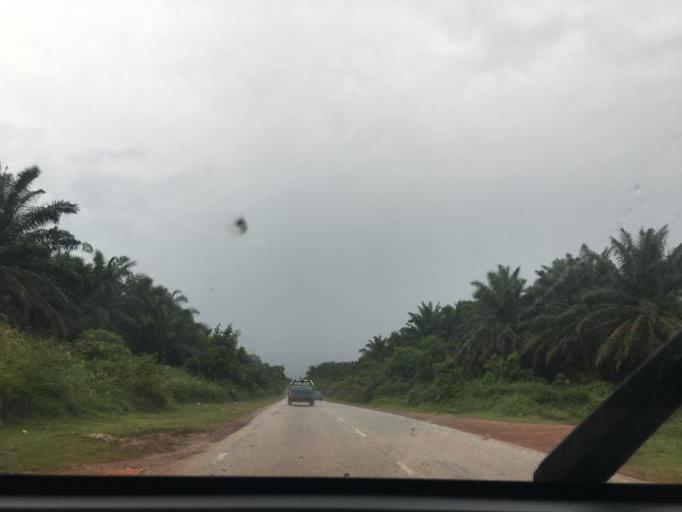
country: MY
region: Kedah
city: Sungai Petani
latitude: 5.6297
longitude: 100.6326
